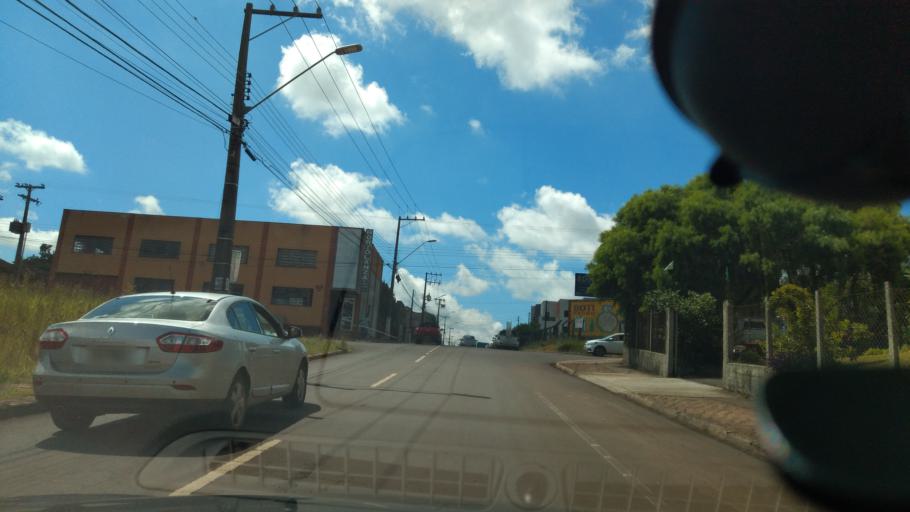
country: BR
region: Parana
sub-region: Guarapuava
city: Guarapuava
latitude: -25.3852
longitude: -51.4801
